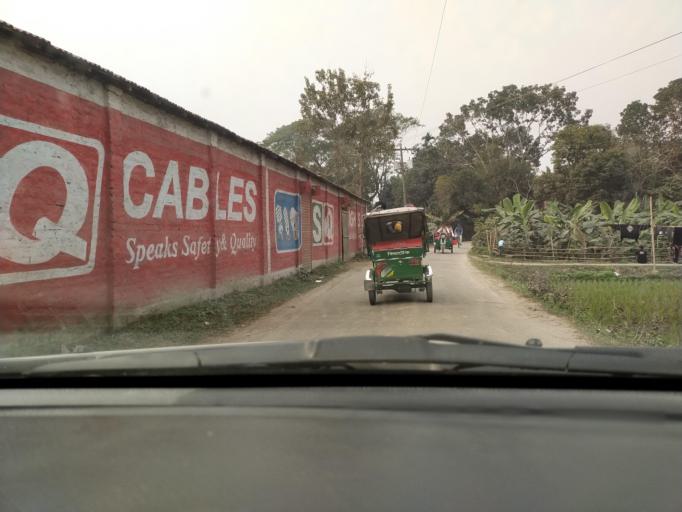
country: BD
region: Dhaka
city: Narsingdi
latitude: 24.0350
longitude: 90.7248
